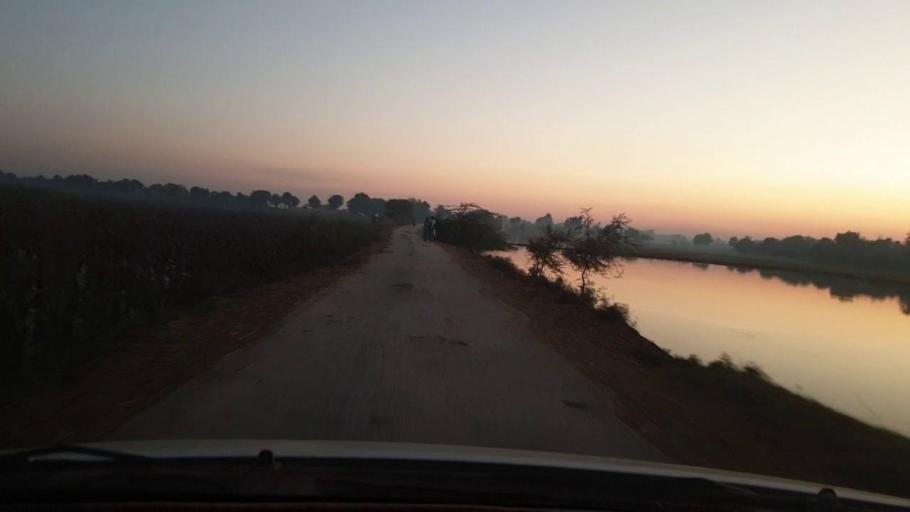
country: PK
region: Sindh
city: Khairpur Nathan Shah
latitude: 27.1408
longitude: 67.7182
